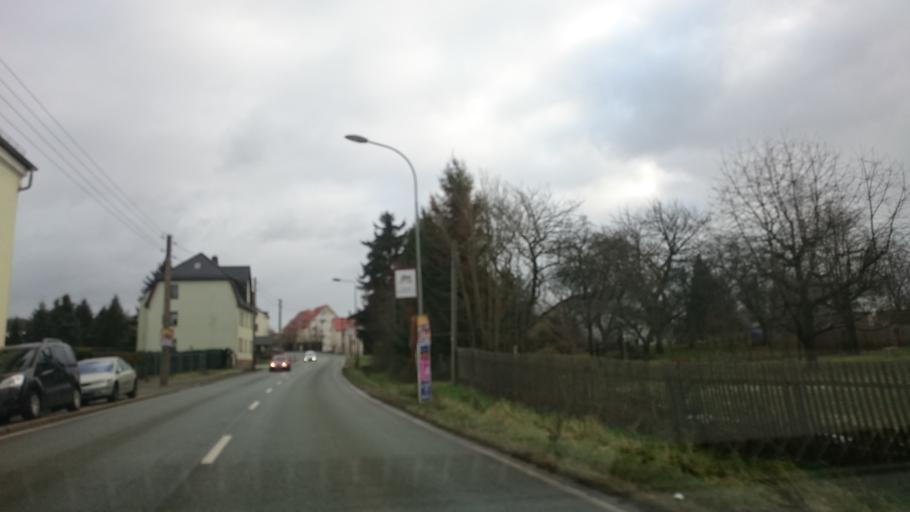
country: DE
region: Saxony
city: Werdau
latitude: 50.7325
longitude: 12.4001
